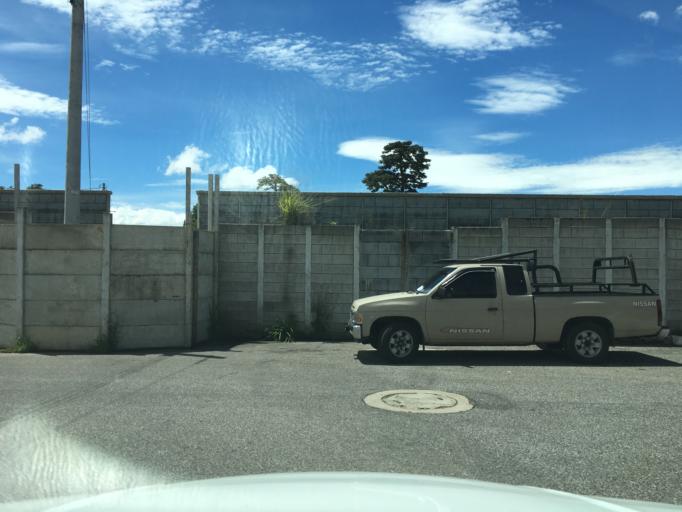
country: GT
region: Guatemala
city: Mixco
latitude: 14.6551
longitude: -90.5646
